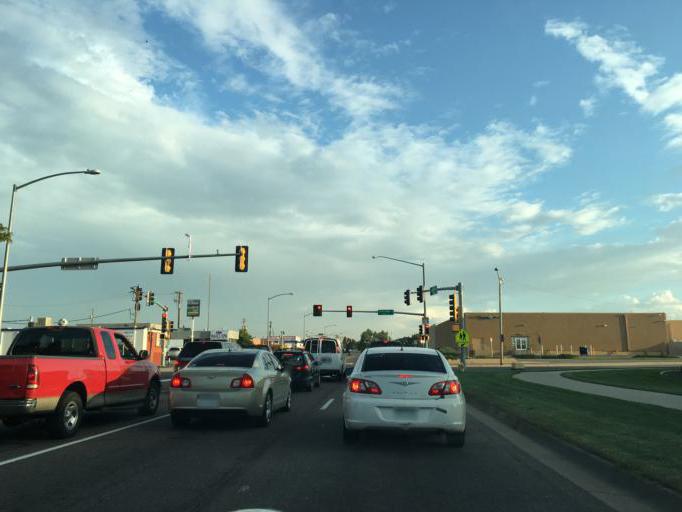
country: US
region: Colorado
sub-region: Adams County
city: Aurora
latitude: 39.7293
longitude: -104.8473
